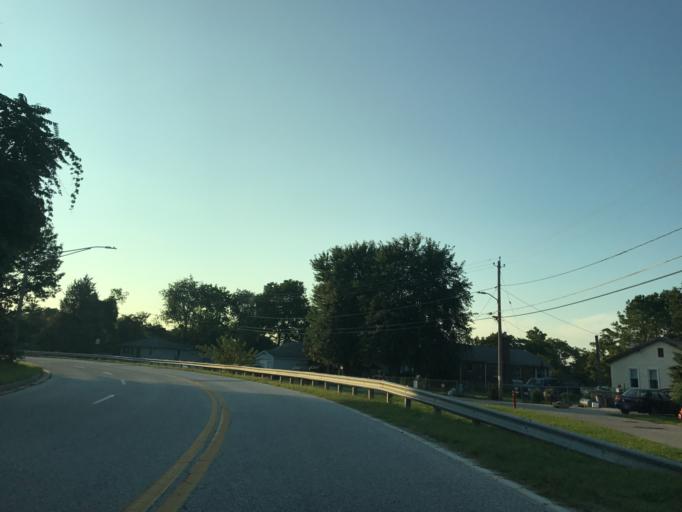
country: US
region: Maryland
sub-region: Baltimore County
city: Essex
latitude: 39.3014
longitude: -76.4946
